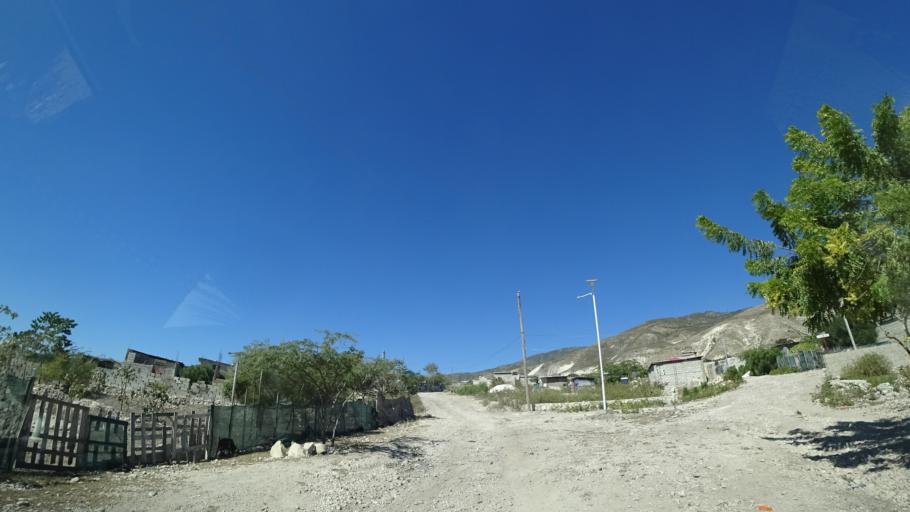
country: HT
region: Ouest
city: Croix des Bouquets
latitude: 18.6700
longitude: -72.2338
